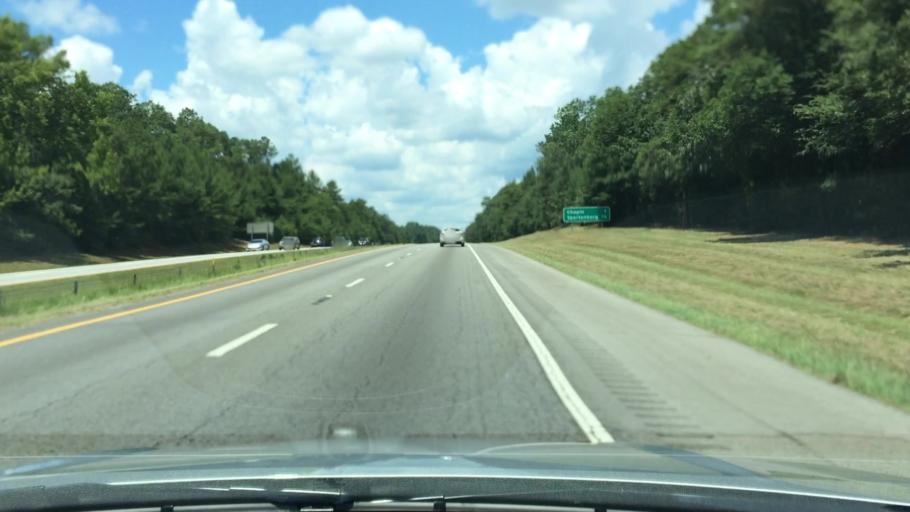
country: US
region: South Carolina
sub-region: Richland County
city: Lake Murray of Richland
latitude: 34.1507
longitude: -81.2488
